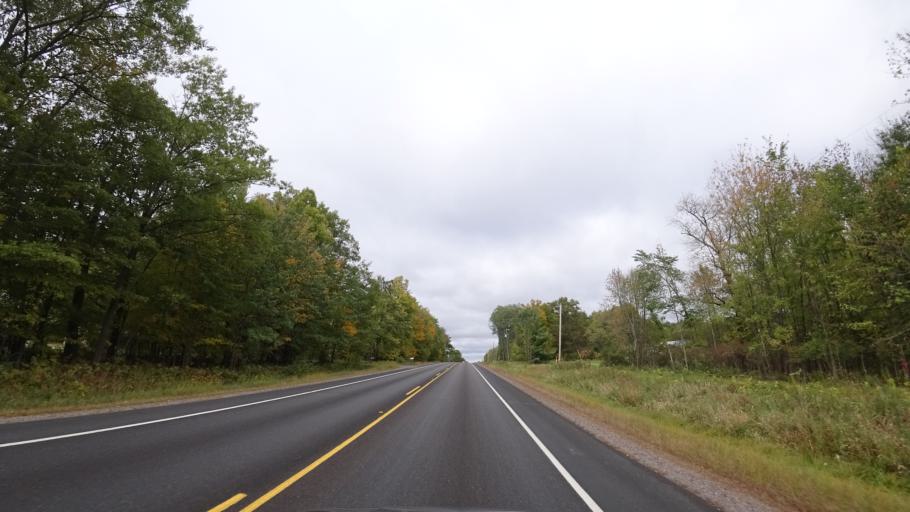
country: US
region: Wisconsin
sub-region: Rusk County
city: Ladysmith
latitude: 45.3404
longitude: -91.1110
